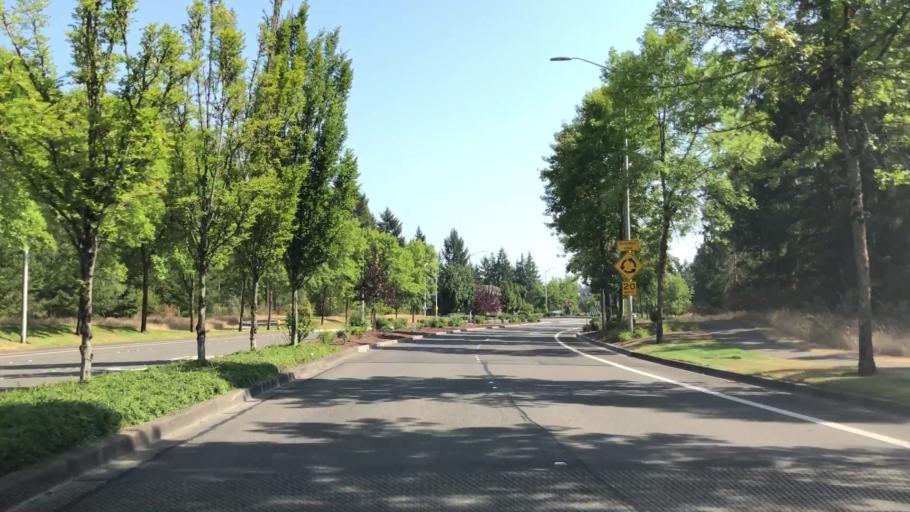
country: US
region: Washington
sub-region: Thurston County
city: Tanglewilde-Thompson Place
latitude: 47.0791
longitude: -122.7527
